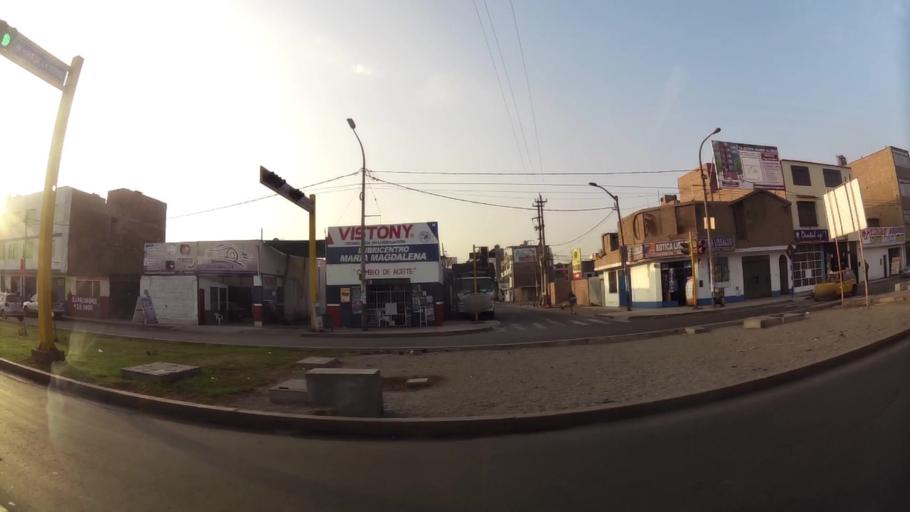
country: PE
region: Lima
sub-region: Lima
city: Independencia
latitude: -11.9910
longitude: -77.0886
